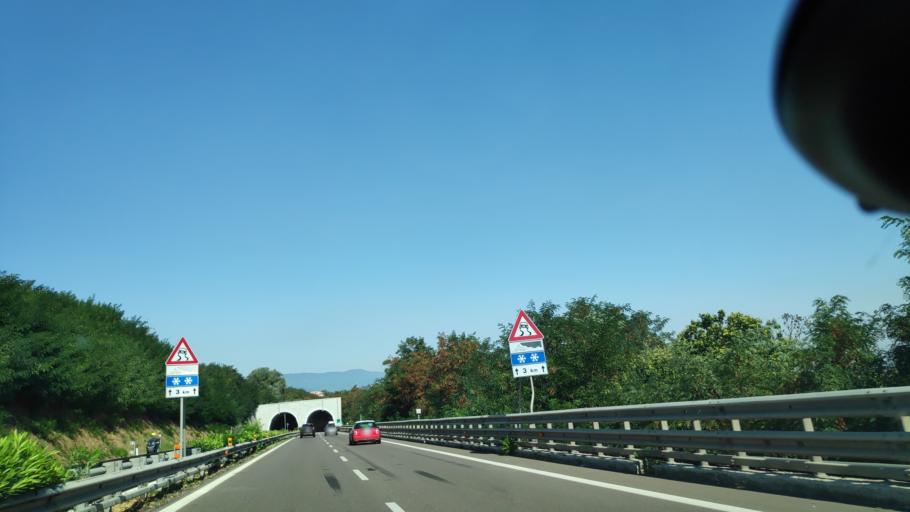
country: IT
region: Calabria
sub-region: Provincia di Cosenza
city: Donnici Inferiore
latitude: 39.2419
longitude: 16.2873
